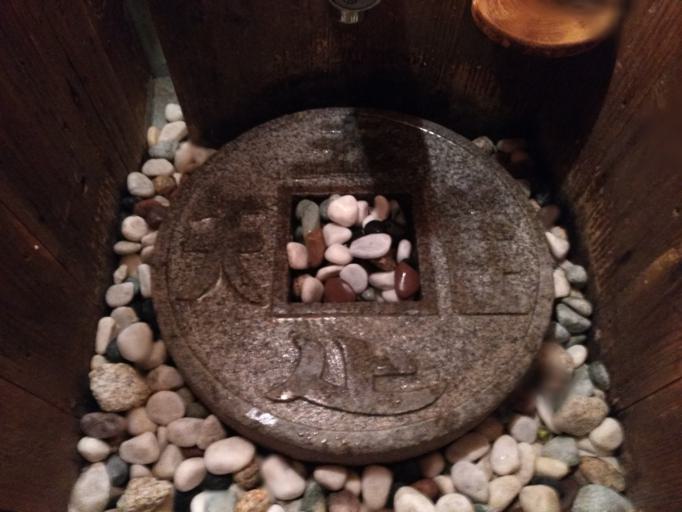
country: JP
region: Tokyo
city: Tokyo
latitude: 35.6992
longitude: 139.7452
